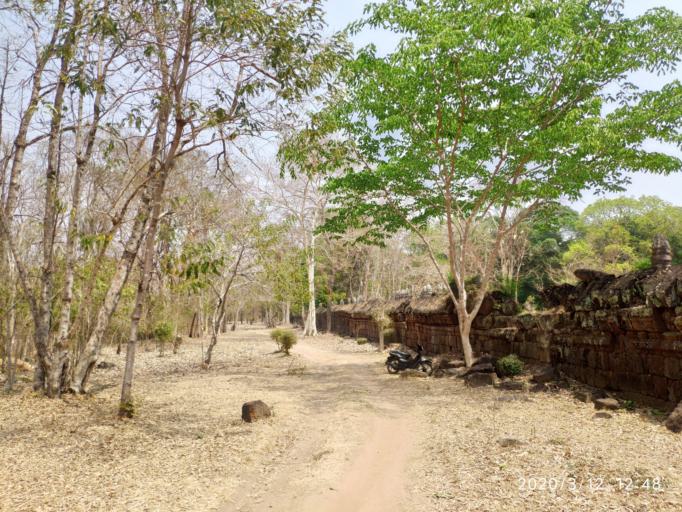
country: KH
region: Preah Vihear
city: Tbeng Meanchey
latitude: 13.7840
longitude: 104.5375
